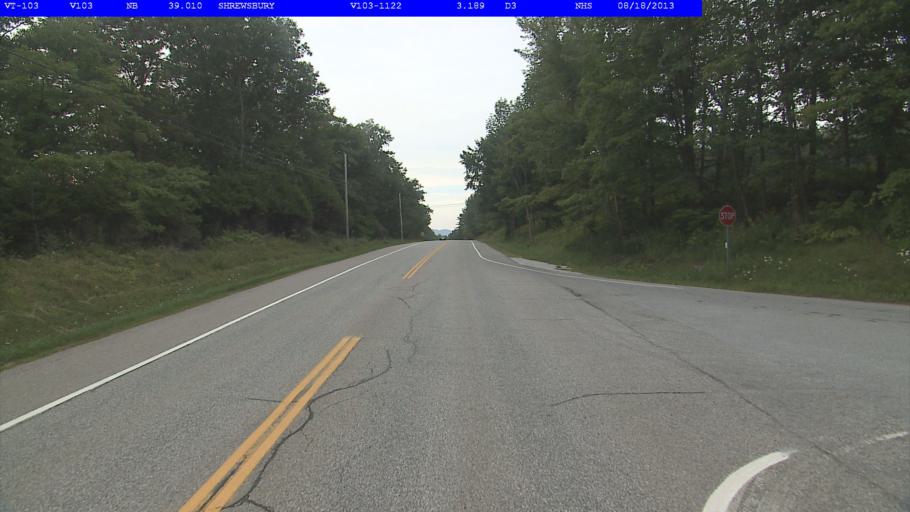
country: US
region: Vermont
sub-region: Rutland County
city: Rutland
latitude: 43.5140
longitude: -72.9159
